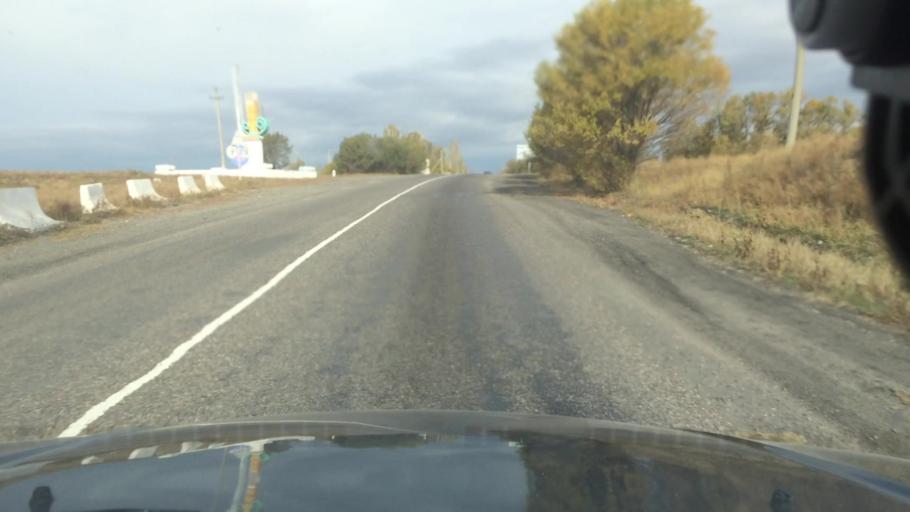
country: KG
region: Ysyk-Koel
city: Karakol
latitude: 42.5980
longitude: 78.3754
